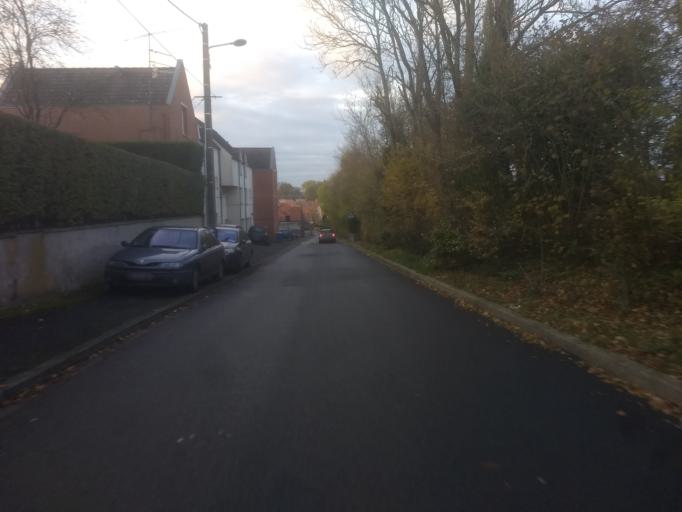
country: FR
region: Nord-Pas-de-Calais
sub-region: Departement du Pas-de-Calais
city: Dainville
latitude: 50.2789
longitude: 2.7277
